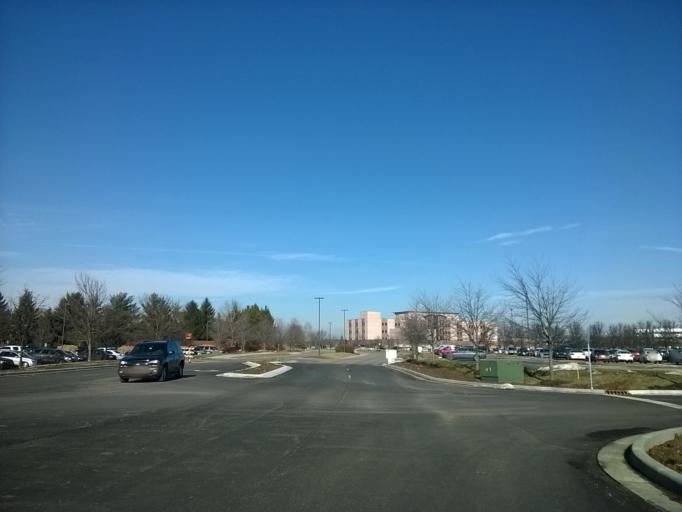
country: US
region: Indiana
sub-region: Marion County
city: Meridian Hills
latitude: 39.9364
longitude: -86.1615
